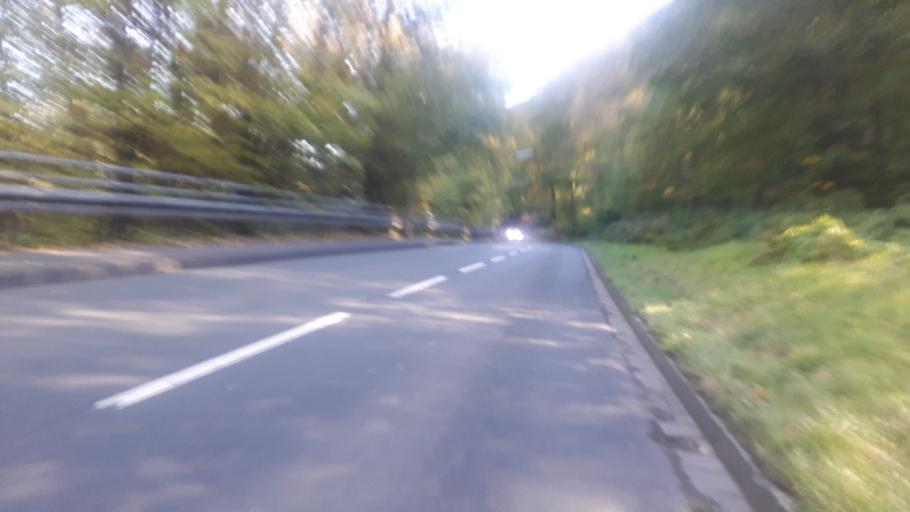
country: DE
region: Rheinland-Pfalz
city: Wissen
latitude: 50.7802
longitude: 7.7437
